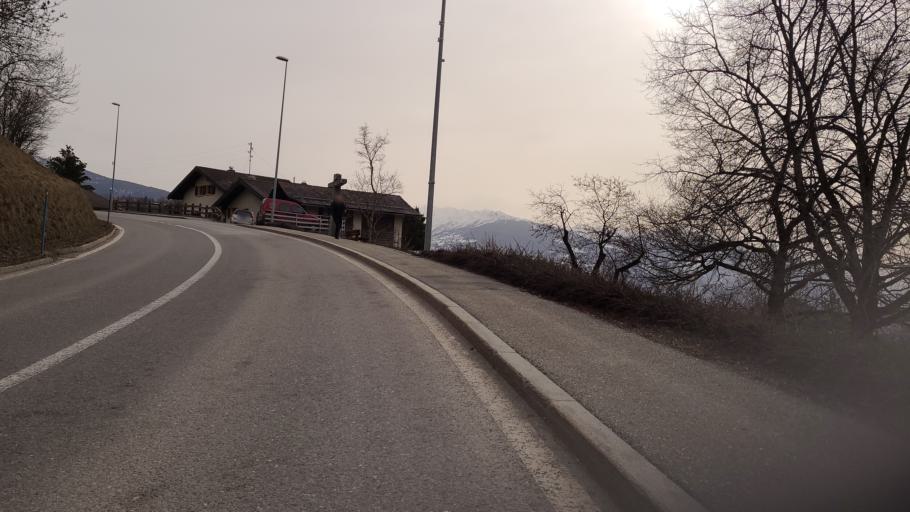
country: CH
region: Valais
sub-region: Sierre District
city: Lens
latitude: 46.2906
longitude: 7.4400
